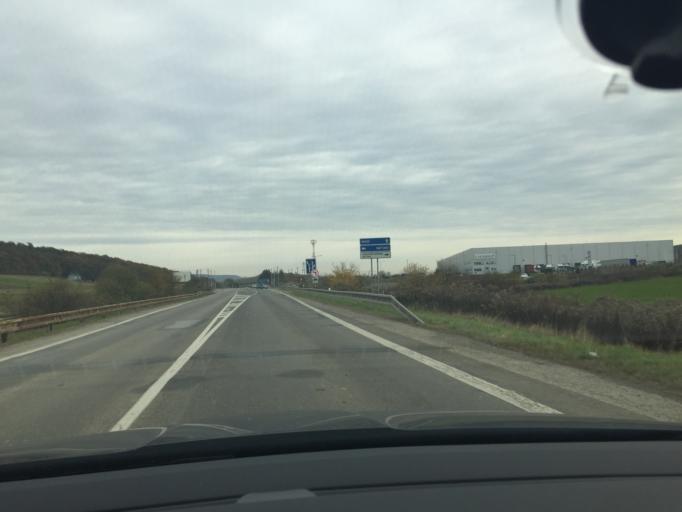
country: SK
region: Presovsky
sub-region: Okres Presov
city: Presov
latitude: 49.0026
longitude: 21.1883
